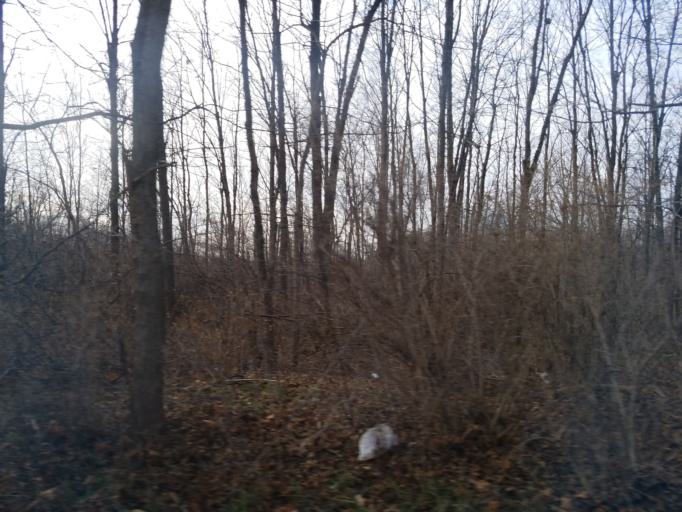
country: US
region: Illinois
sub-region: Will County
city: Homer Glen
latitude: 41.5578
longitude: -87.9432
